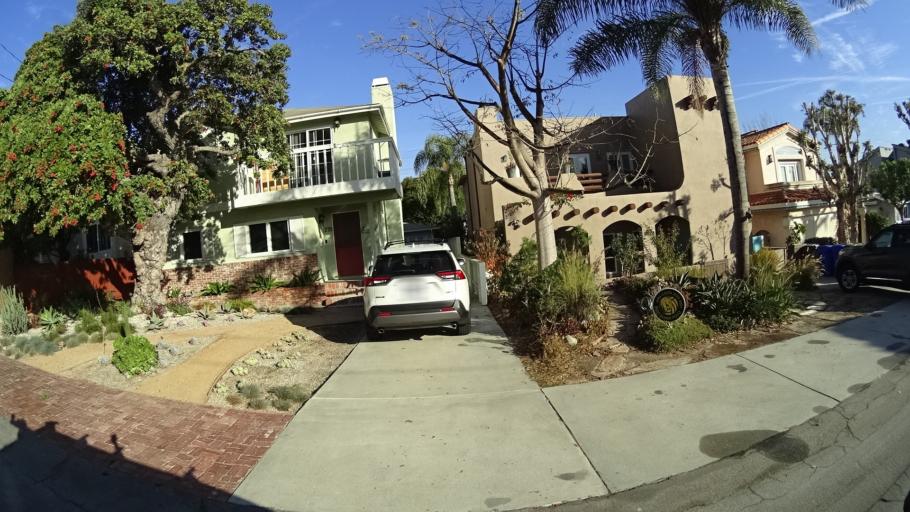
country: US
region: California
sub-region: Los Angeles County
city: Manhattan Beach
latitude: 33.9009
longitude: -118.4061
